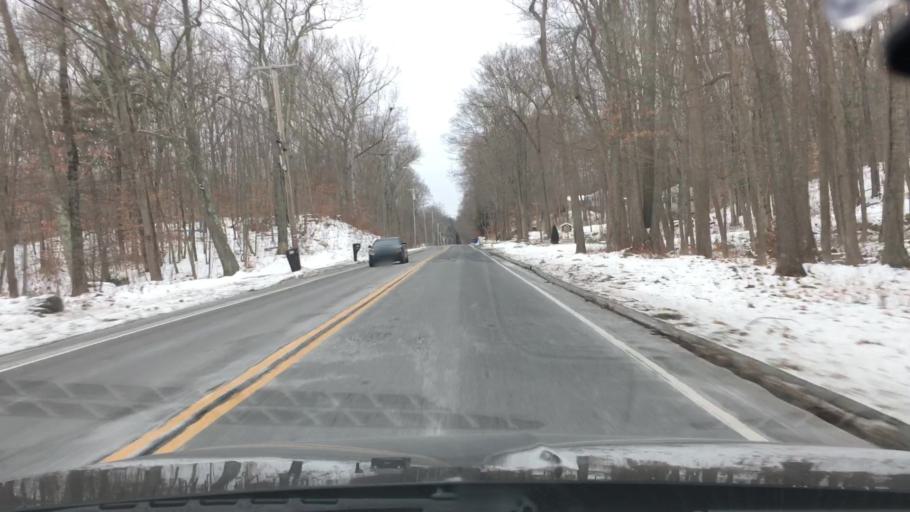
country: US
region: Connecticut
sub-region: Tolland County
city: Tolland
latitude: 41.8439
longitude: -72.3228
